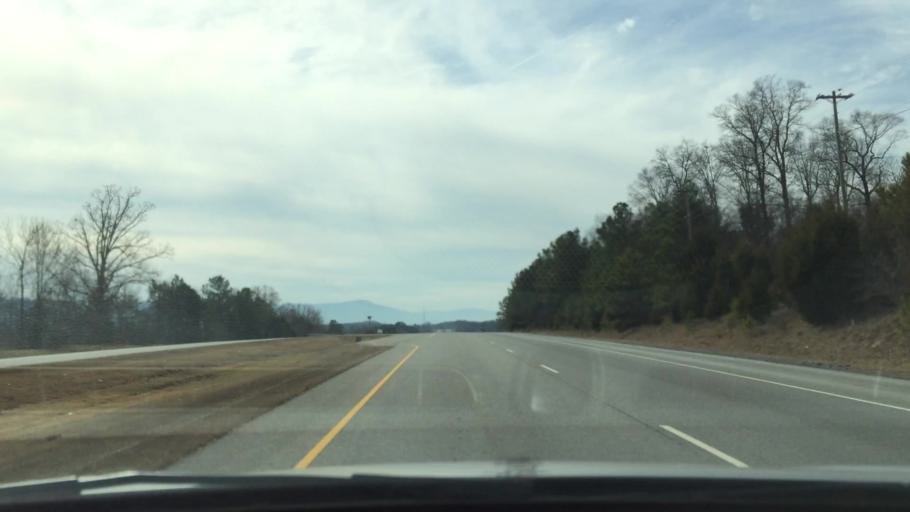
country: US
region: Tennessee
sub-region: McMinn County
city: Englewood
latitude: 35.3837
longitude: -84.5061
